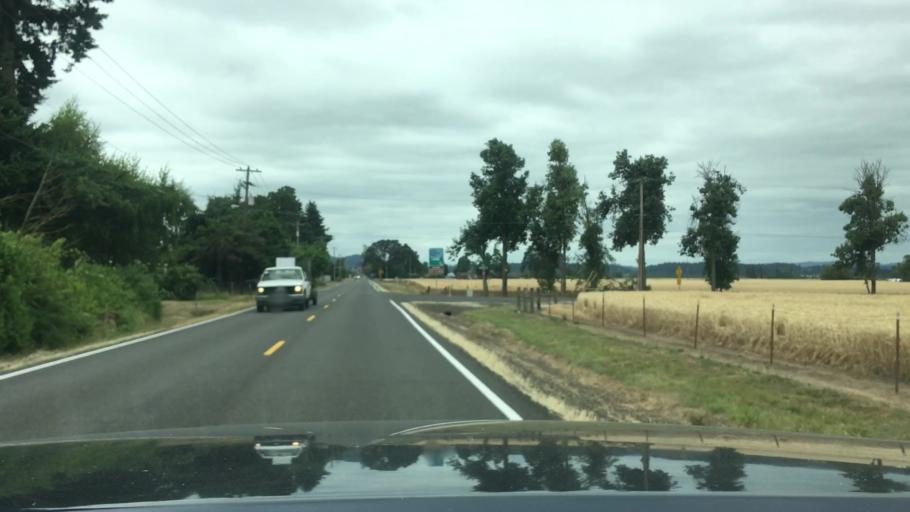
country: US
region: Oregon
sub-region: Lane County
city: Junction City
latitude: 44.1071
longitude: -123.2084
